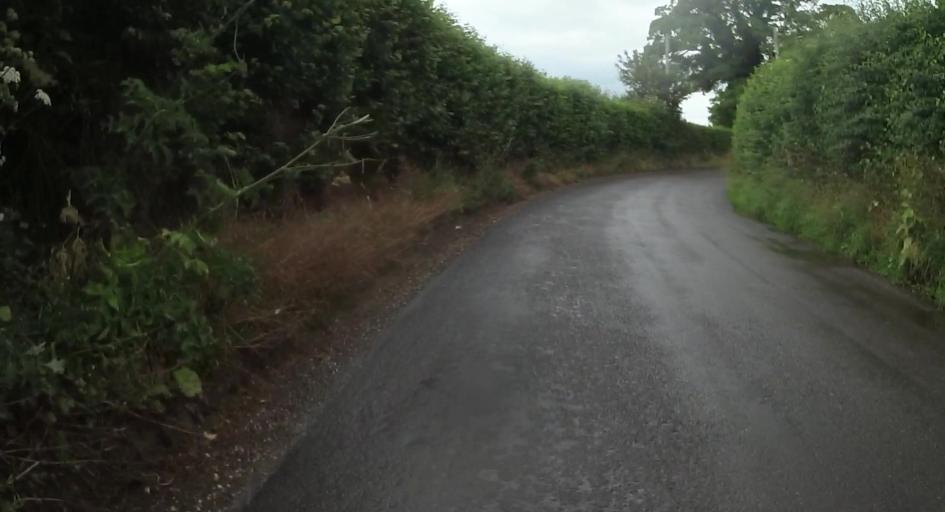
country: GB
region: England
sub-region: Hampshire
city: Long Sutton
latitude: 51.2199
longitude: -0.9215
